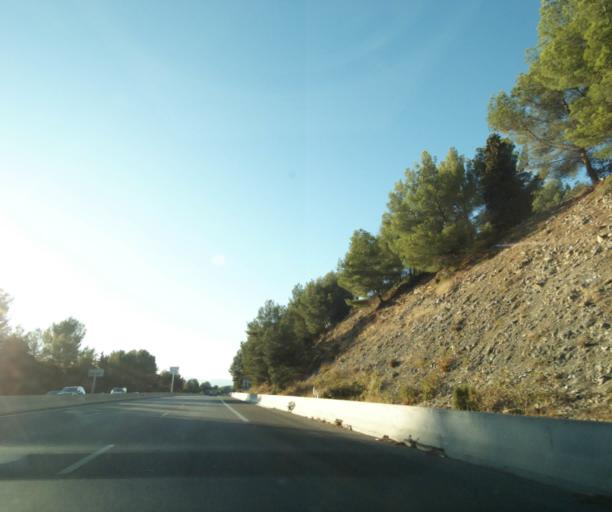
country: FR
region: Provence-Alpes-Cote d'Azur
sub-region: Departement du Var
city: Saint-Cyr-sur-Mer
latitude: 43.1929
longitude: 5.6808
